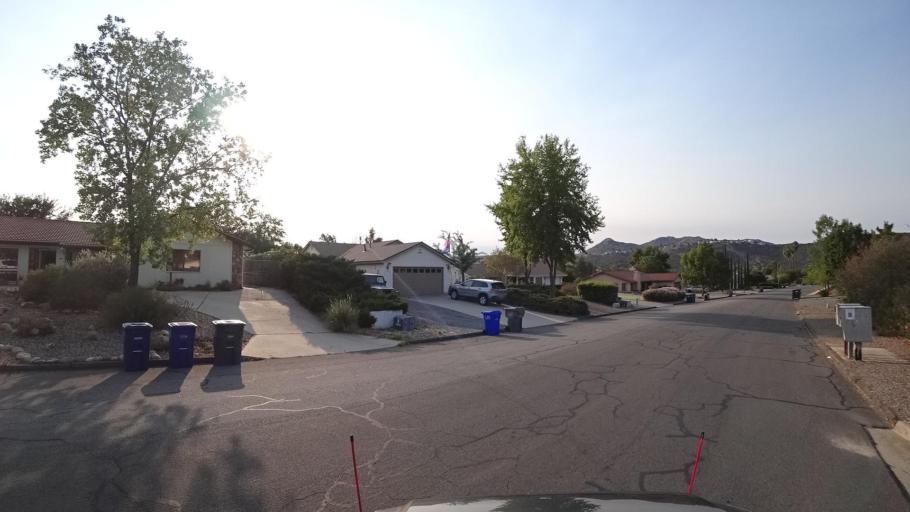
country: US
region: California
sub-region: San Diego County
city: San Diego Country Estates
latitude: 33.0117
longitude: -116.8230
